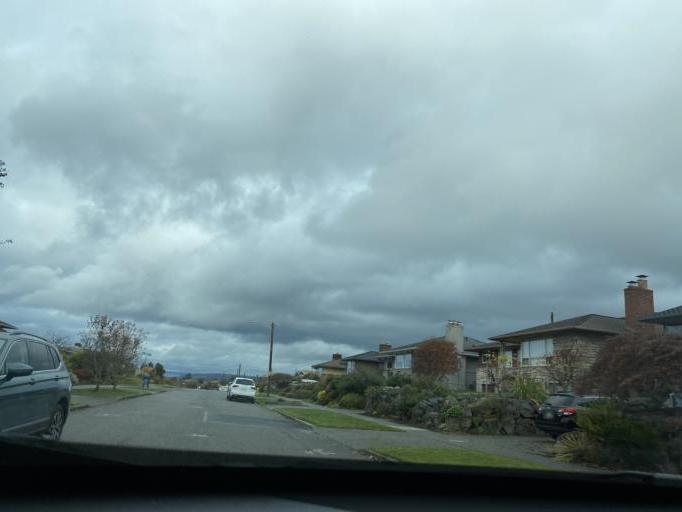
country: US
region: Washington
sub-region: King County
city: Shoreline
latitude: 47.6924
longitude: -122.3850
